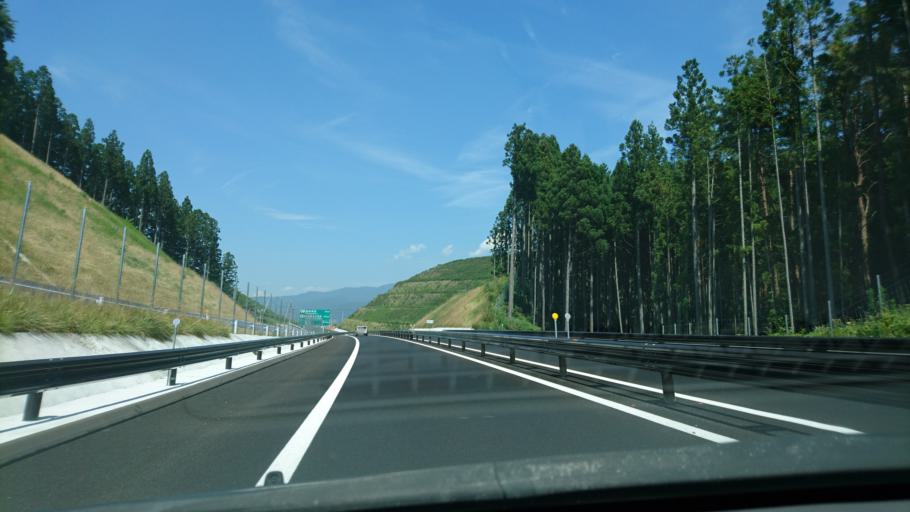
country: JP
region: Iwate
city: Ofunato
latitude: 38.9967
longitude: 141.6147
